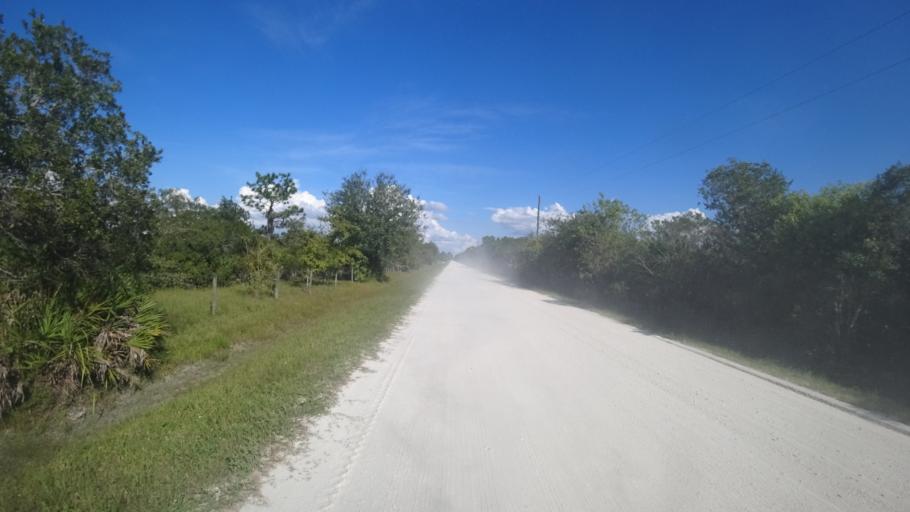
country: US
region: Florida
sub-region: Sarasota County
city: The Meadows
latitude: 27.4227
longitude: -82.2700
